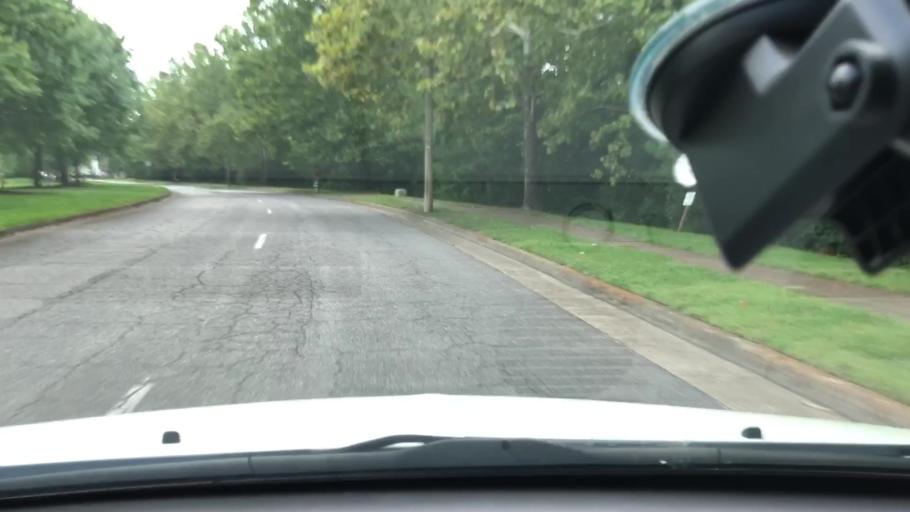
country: US
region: Virginia
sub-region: City of Chesapeake
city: Chesapeake
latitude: 36.7163
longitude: -76.2887
